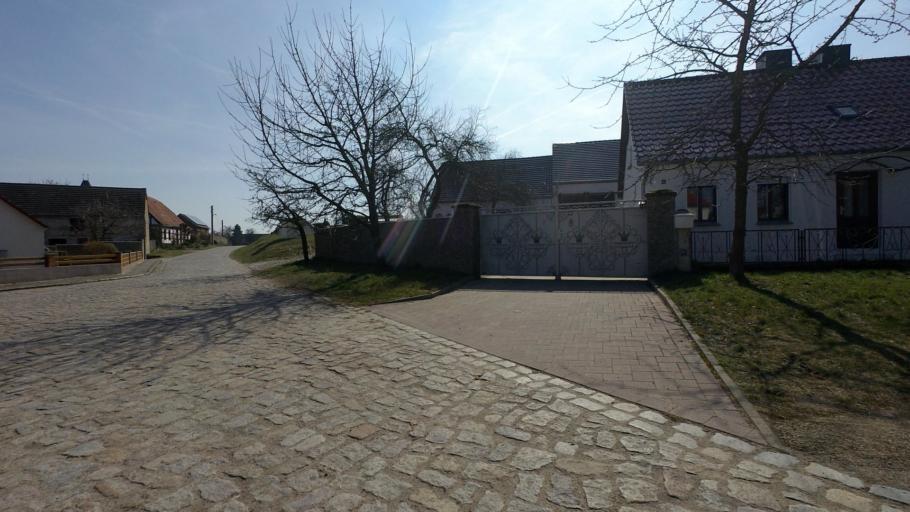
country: DE
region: Brandenburg
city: Golssen
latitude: 51.9847
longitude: 13.5394
